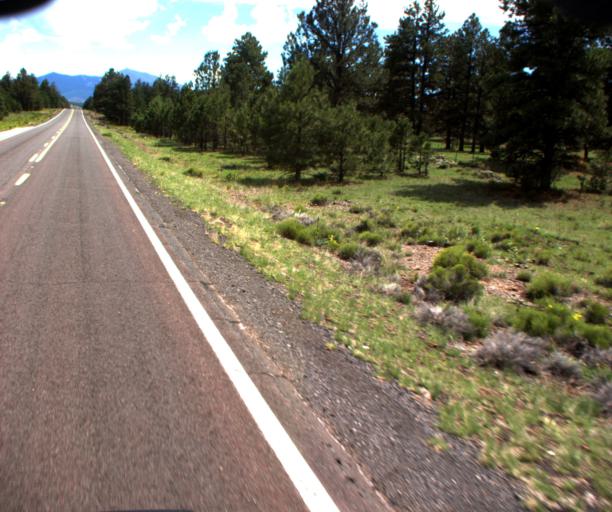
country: US
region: Arizona
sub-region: Coconino County
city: Parks
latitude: 35.4720
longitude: -111.7910
